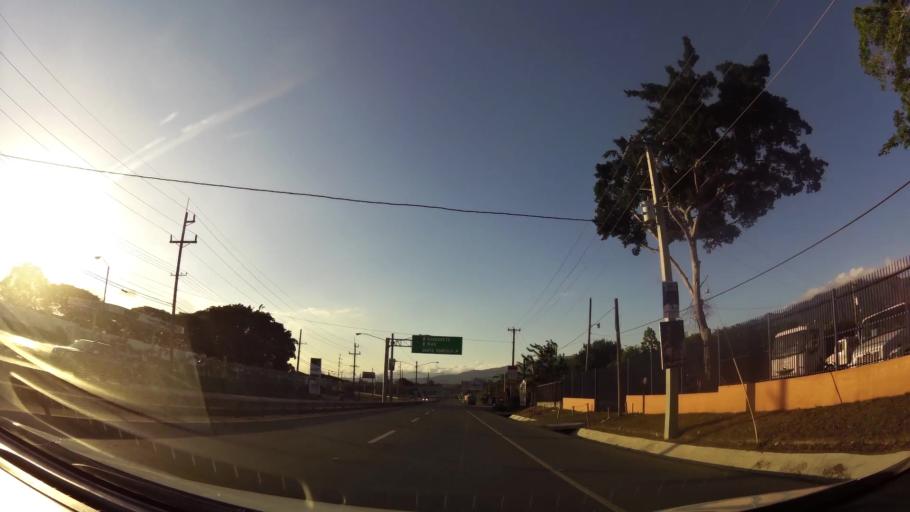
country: DO
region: Santiago
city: Palmar Arriba
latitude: 19.5148
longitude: -70.7611
